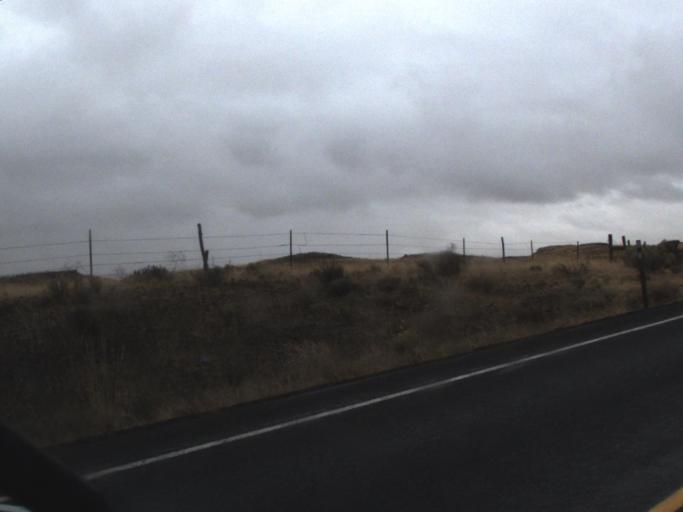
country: US
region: Washington
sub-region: Spokane County
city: Medical Lake
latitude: 47.2873
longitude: -117.9637
